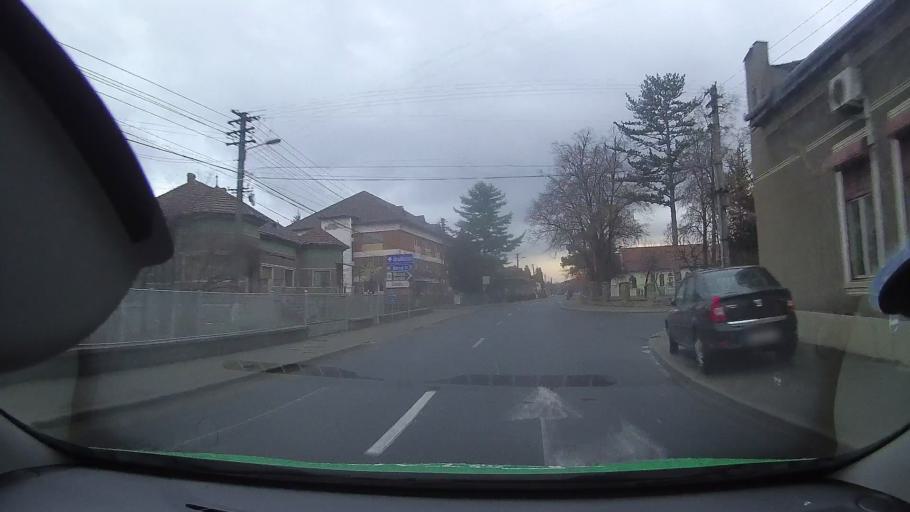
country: RO
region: Hunedoara
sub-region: Municipiul Brad
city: Brad
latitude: 46.1297
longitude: 22.7844
